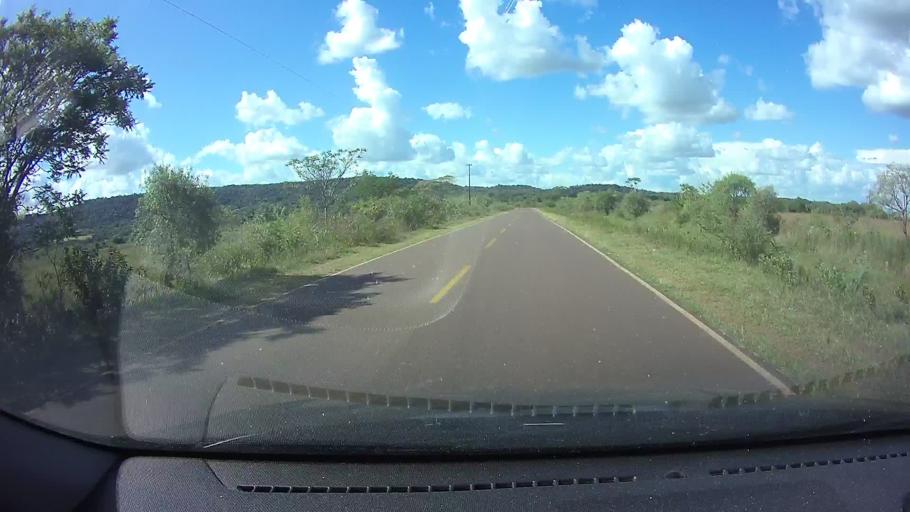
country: PY
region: Paraguari
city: Sapucai
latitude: -25.6823
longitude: -56.8631
